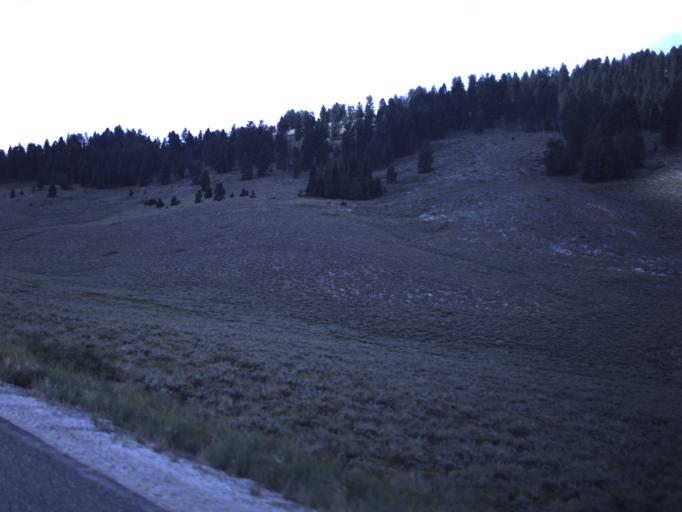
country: US
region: Idaho
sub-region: Bear Lake County
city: Paris
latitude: 41.9431
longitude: -111.4816
